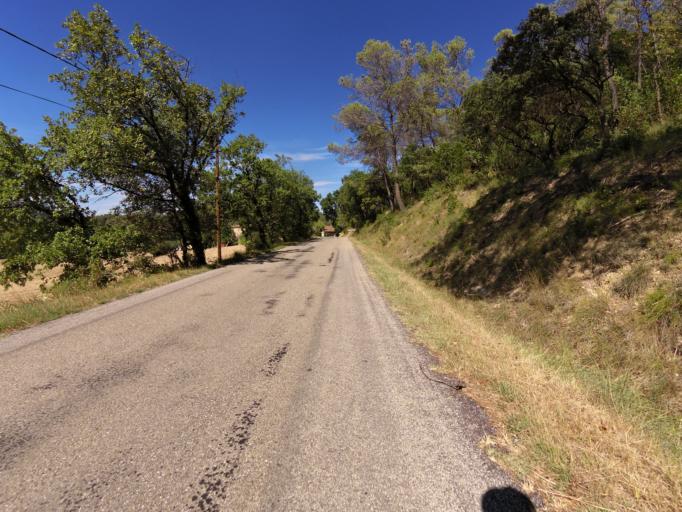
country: FR
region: Languedoc-Roussillon
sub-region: Departement du Gard
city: Quissac
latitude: 43.9153
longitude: 4.0491
